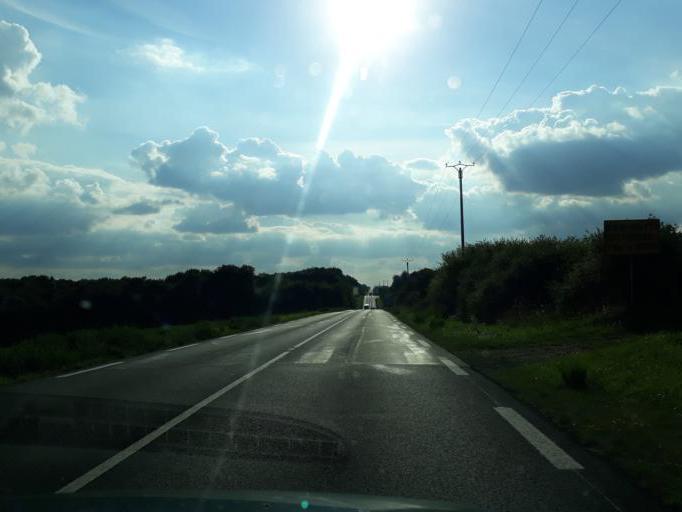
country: FR
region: Centre
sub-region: Departement du Loir-et-Cher
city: La Ville-aux-Clercs
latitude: 47.8931
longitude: 1.1182
